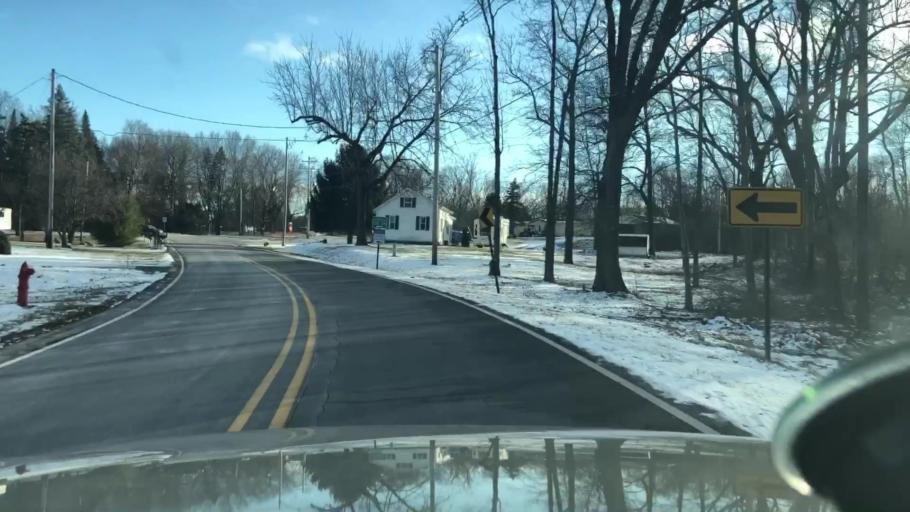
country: US
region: Michigan
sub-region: Jackson County
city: Vandercook Lake
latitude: 42.1612
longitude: -84.4527
